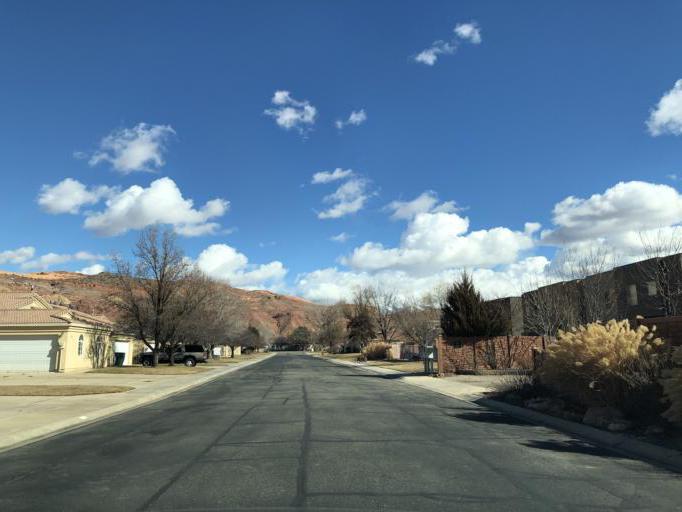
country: US
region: Utah
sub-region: Grand County
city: Moab
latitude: 38.5807
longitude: -109.5638
